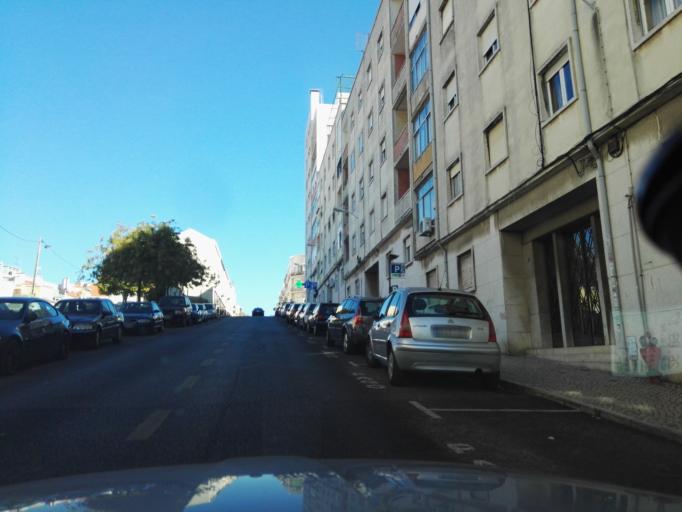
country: PT
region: Setubal
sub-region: Almada
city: Cacilhas
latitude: 38.7154
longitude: -9.1695
